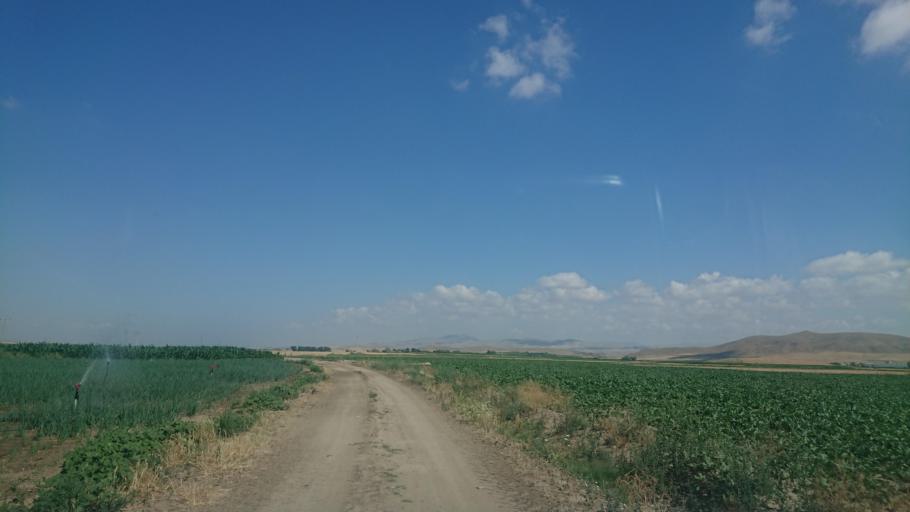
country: TR
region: Aksaray
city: Sariyahsi
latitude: 38.9841
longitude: 33.9066
